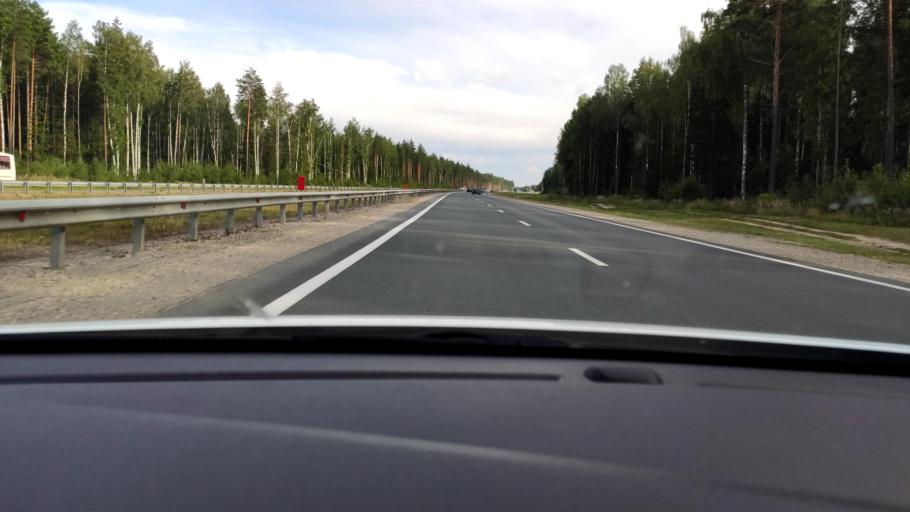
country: RU
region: Mariy-El
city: Surok
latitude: 56.5254
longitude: 48.0068
